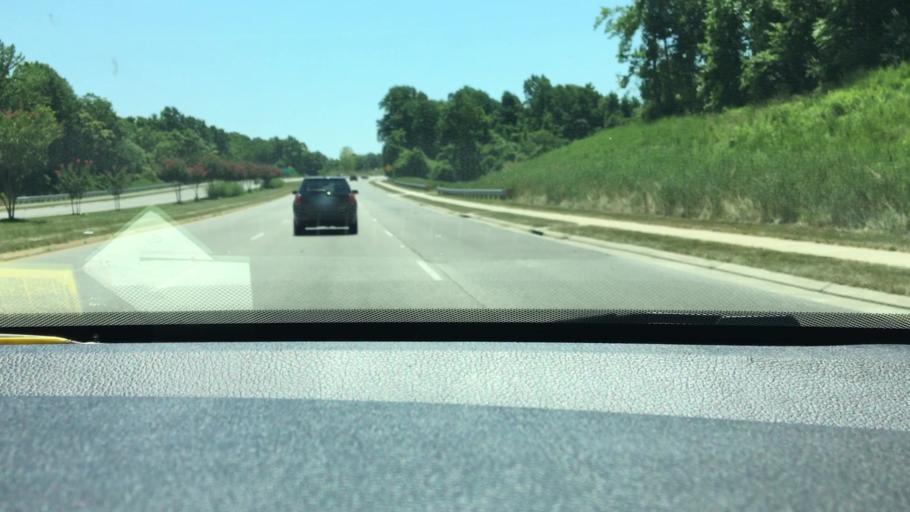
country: US
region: Virginia
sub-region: Prince William County
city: Dale City
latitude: 38.6562
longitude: -77.3199
